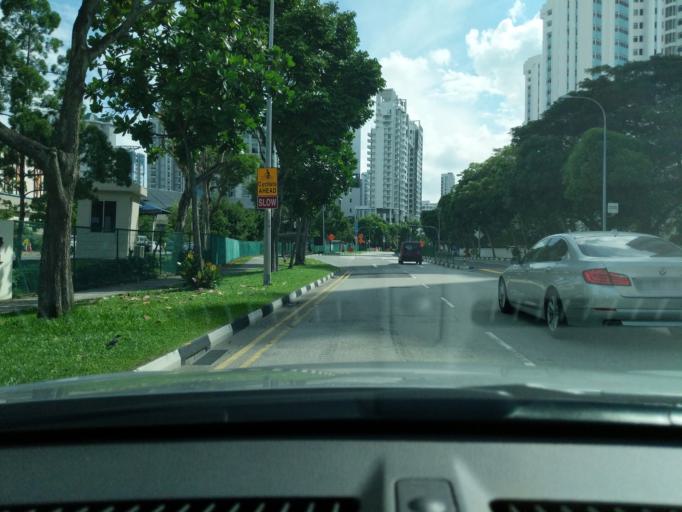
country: SG
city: Singapore
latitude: 1.2979
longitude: 103.8817
